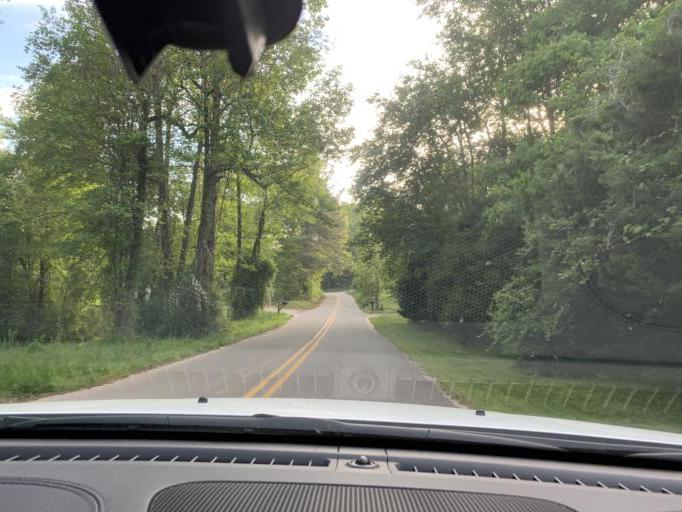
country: US
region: Georgia
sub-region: Dawson County
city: Dawsonville
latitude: 34.3337
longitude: -84.1686
